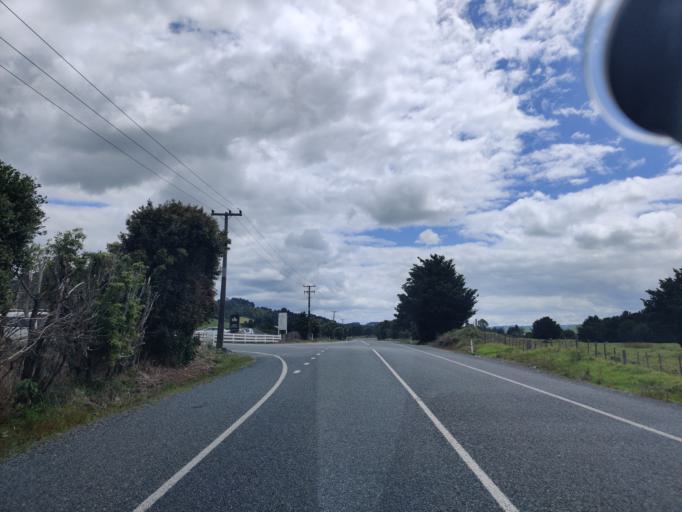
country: NZ
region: Northland
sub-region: Far North District
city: Kerikeri
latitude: -35.2935
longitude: 173.9843
